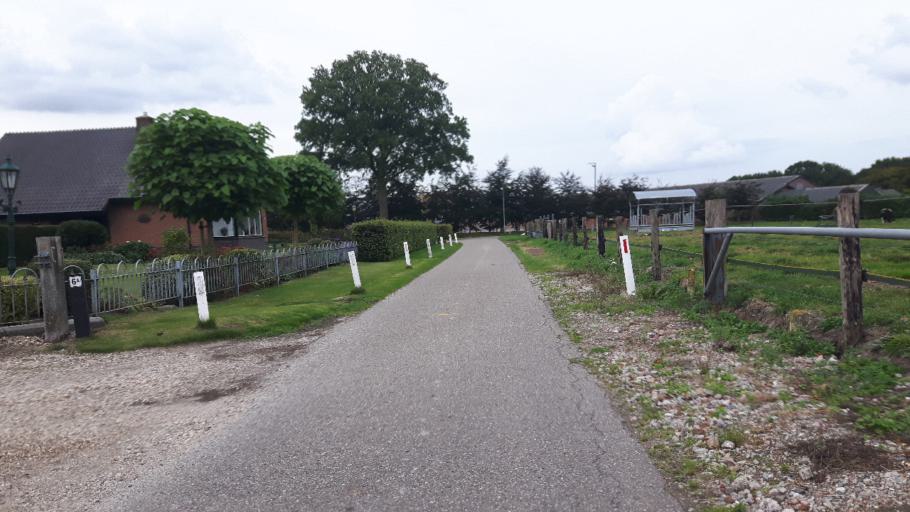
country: NL
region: Gelderland
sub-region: Gemeente Barneveld
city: Terschuur
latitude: 52.1974
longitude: 5.5555
